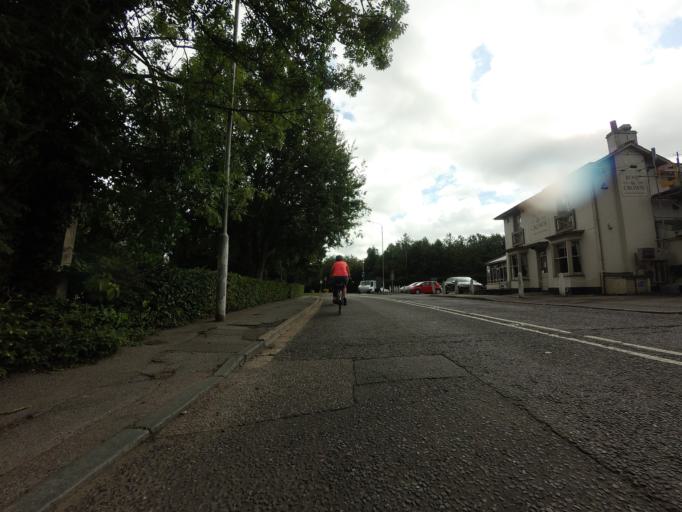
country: GB
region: England
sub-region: Kent
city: Shoreham
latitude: 51.3004
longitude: 0.1607
